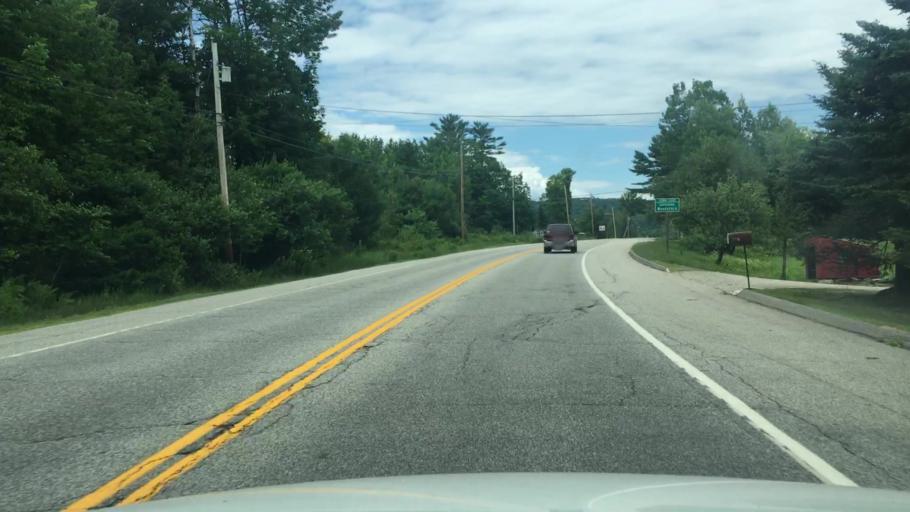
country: US
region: Maine
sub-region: Oxford County
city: West Paris
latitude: 44.3440
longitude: -70.5624
